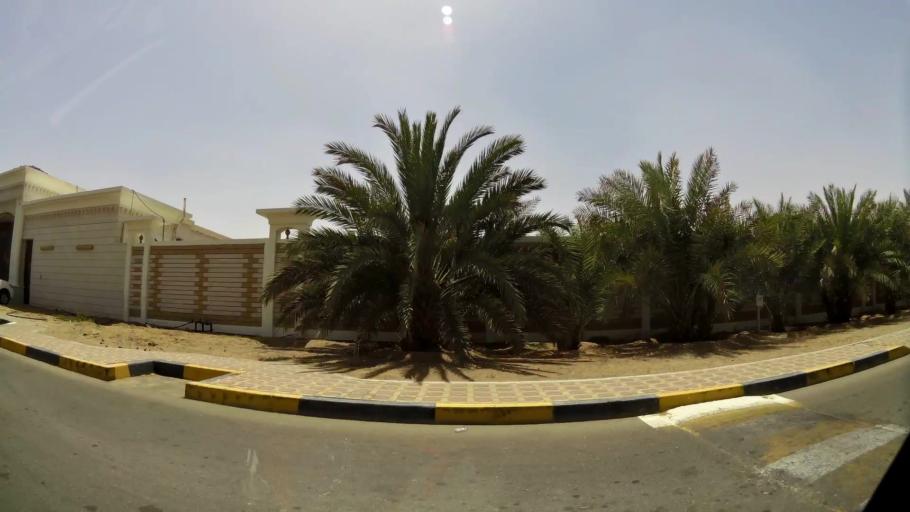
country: AE
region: Abu Dhabi
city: Al Ain
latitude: 24.2557
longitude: 55.6992
